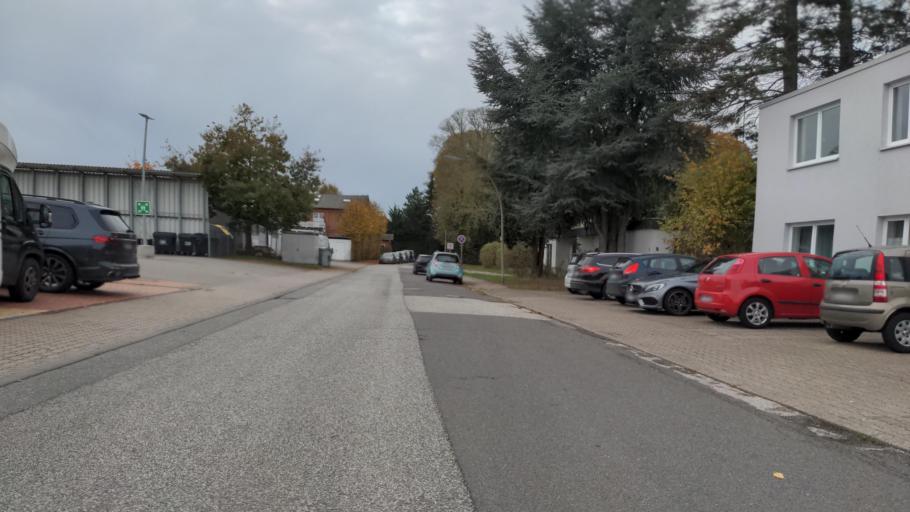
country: DE
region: Schleswig-Holstein
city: Bad Schwartau
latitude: 53.9126
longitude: 10.6702
